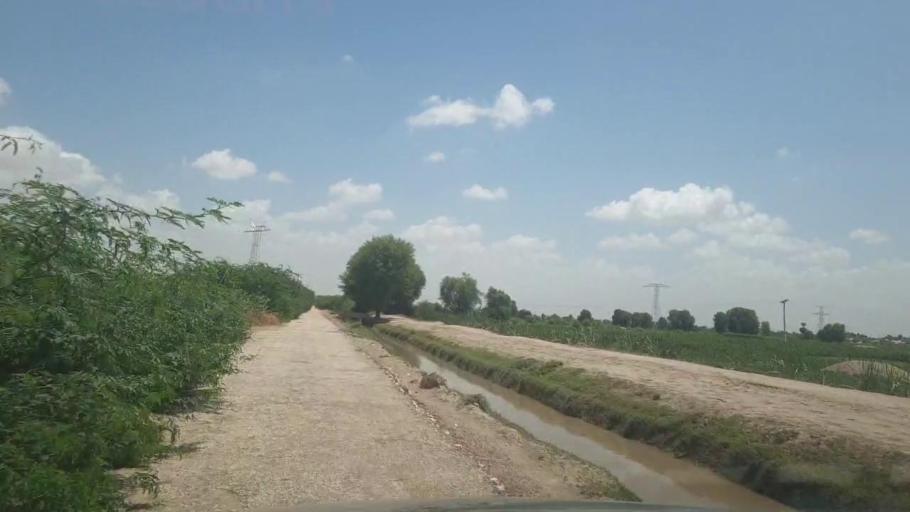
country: PK
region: Sindh
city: Kot Diji
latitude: 27.2594
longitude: 69.0440
